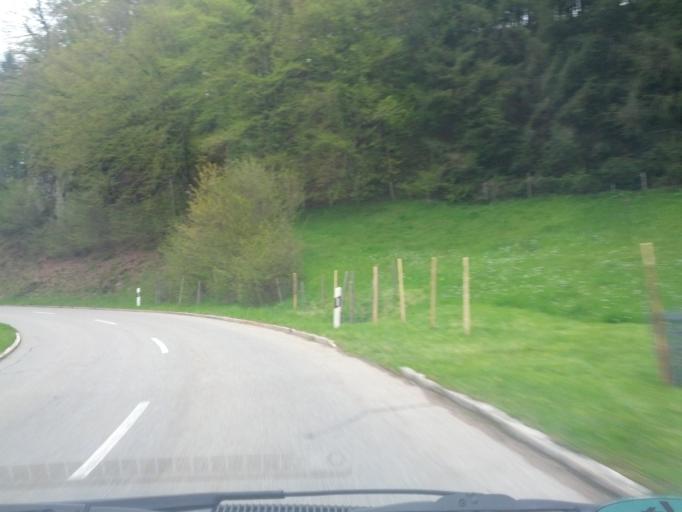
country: DE
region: Baden-Wuerttemberg
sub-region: Freiburg Region
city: Zell im Wiesental
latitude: 47.7375
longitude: 7.8131
